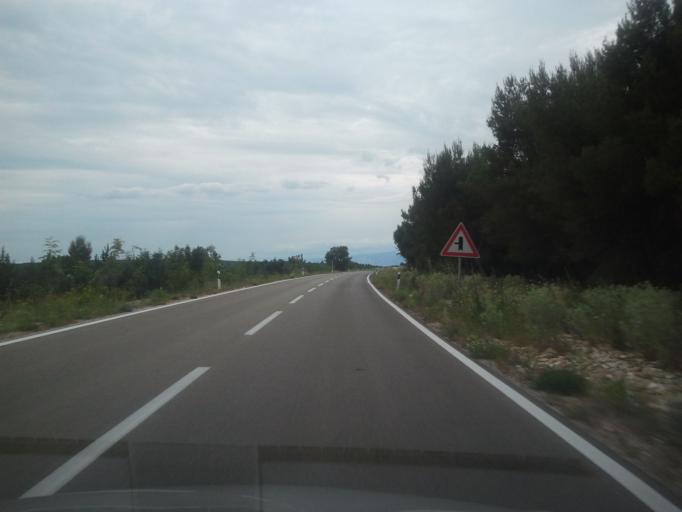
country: HR
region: Zadarska
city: Benkovac
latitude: 44.0709
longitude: 15.6029
